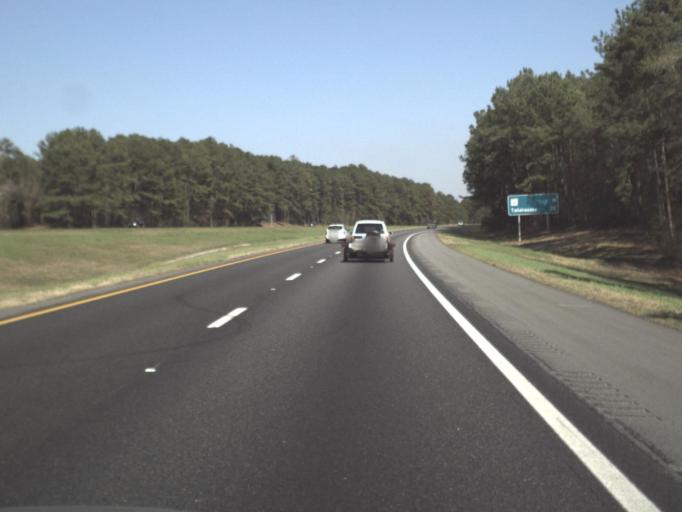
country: US
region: Florida
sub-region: Gadsden County
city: Chattahoochee
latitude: 30.6214
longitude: -84.8052
